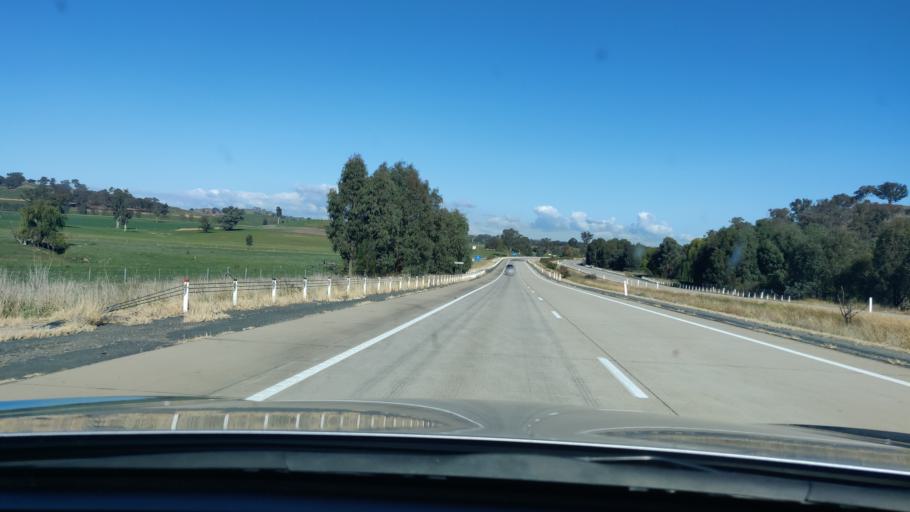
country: AU
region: New South Wales
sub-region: Wagga Wagga
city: Forest Hill
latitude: -35.2377
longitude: 147.7720
